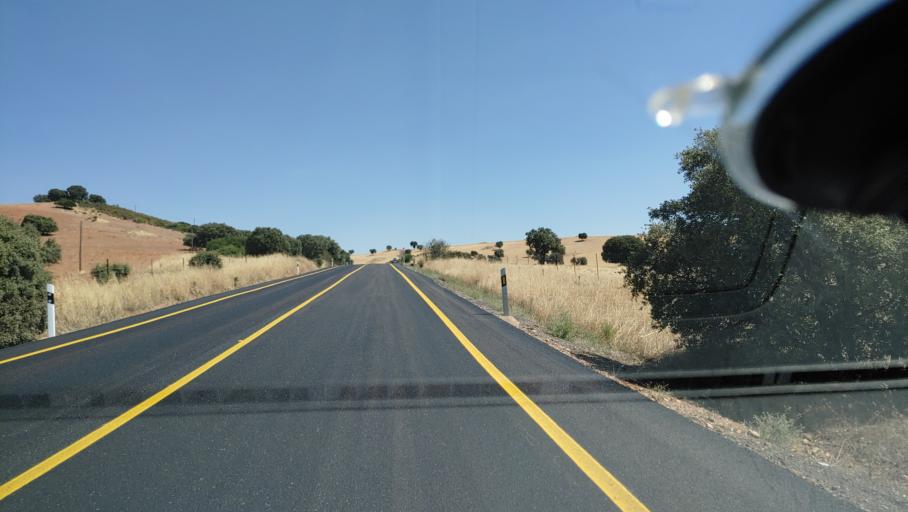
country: ES
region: Castille-La Mancha
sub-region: Provincia de Ciudad Real
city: Saceruela
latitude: 39.0146
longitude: -4.4670
